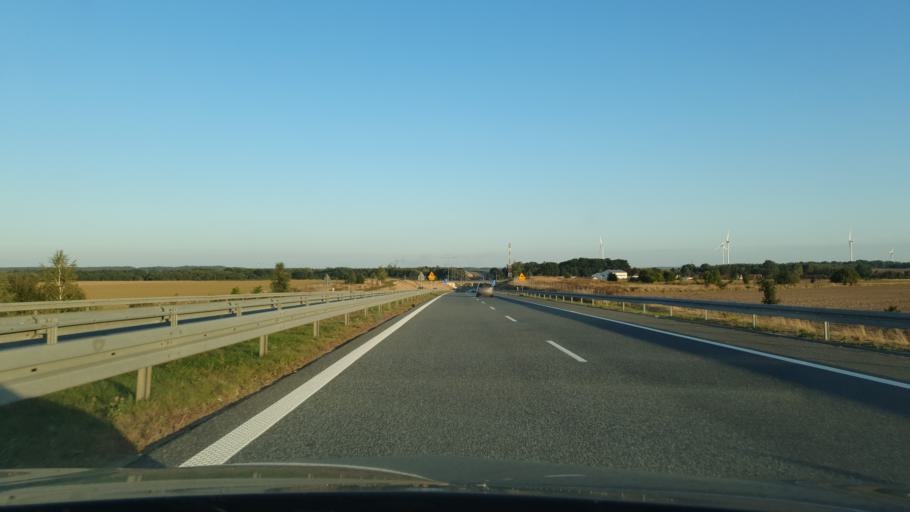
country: PL
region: Pomeranian Voivodeship
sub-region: Powiat slupski
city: Kobylnica
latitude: 54.4365
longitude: 16.9595
